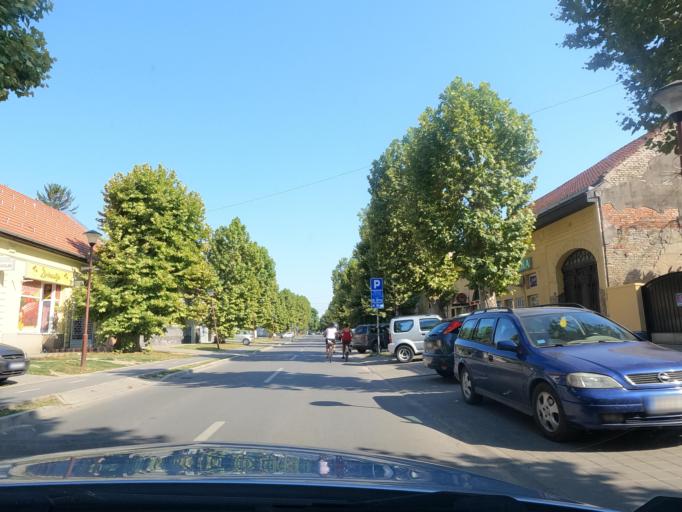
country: RS
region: Autonomna Pokrajina Vojvodina
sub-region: Juznobacki Okrug
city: Becej
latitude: 45.6156
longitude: 20.0452
